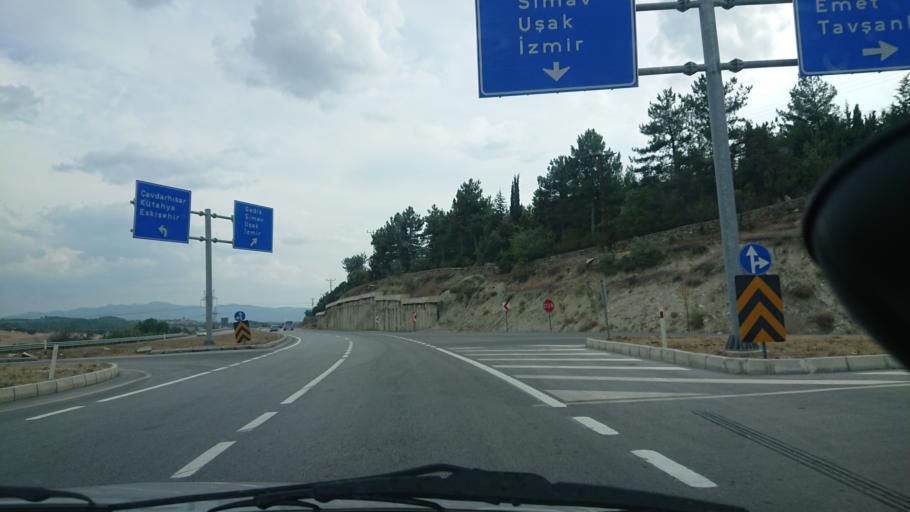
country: TR
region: Kuetahya
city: Gediz
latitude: 39.0314
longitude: 29.4162
